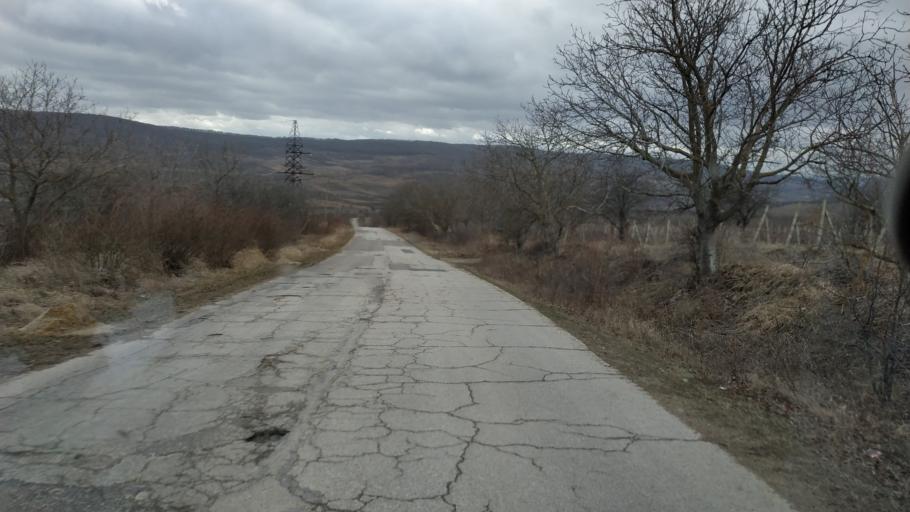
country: MD
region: Stinga Nistrului
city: Bucovat
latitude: 47.2216
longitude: 28.4142
